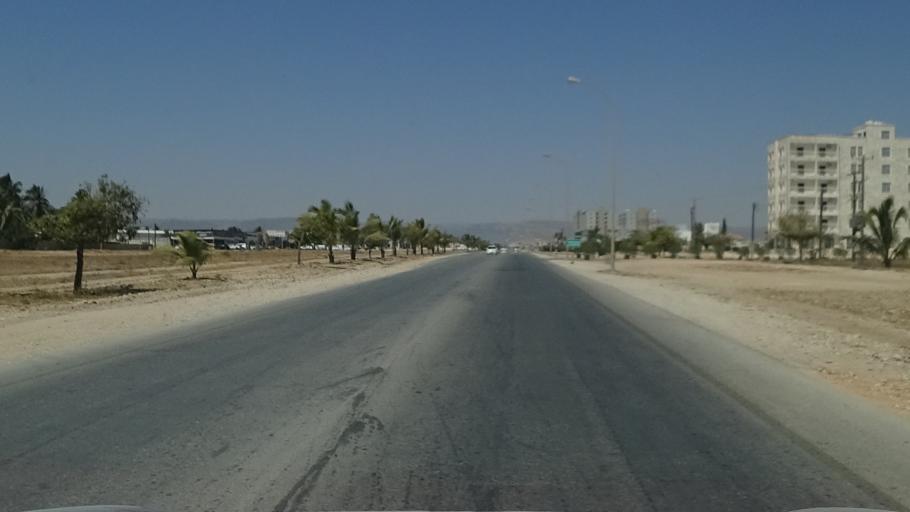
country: OM
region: Zufar
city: Salalah
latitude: 17.0454
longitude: 54.1695
